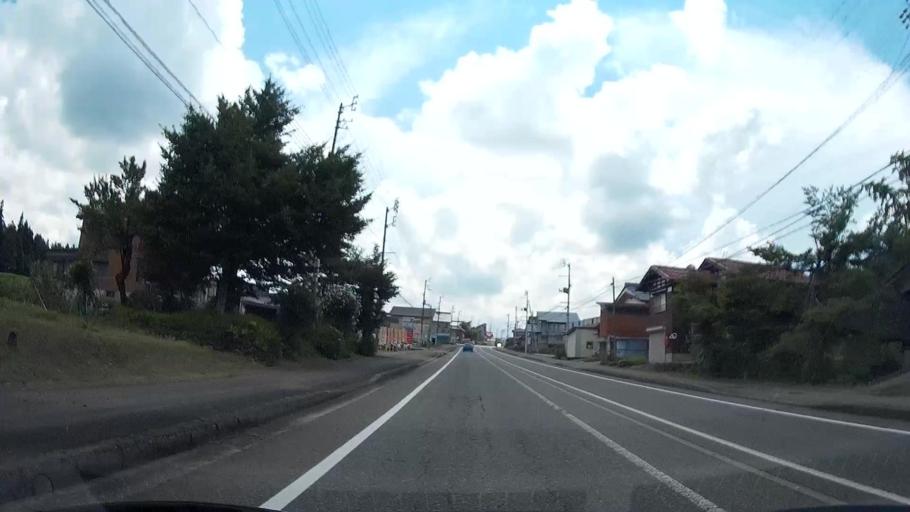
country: JP
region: Niigata
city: Tokamachi
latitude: 37.0362
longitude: 138.6729
